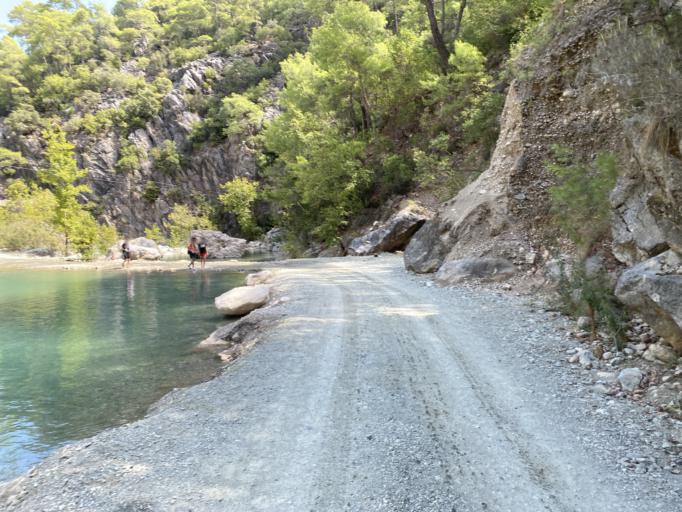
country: TR
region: Antalya
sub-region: Kemer
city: Goeynuek
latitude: 36.6810
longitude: 30.5272
